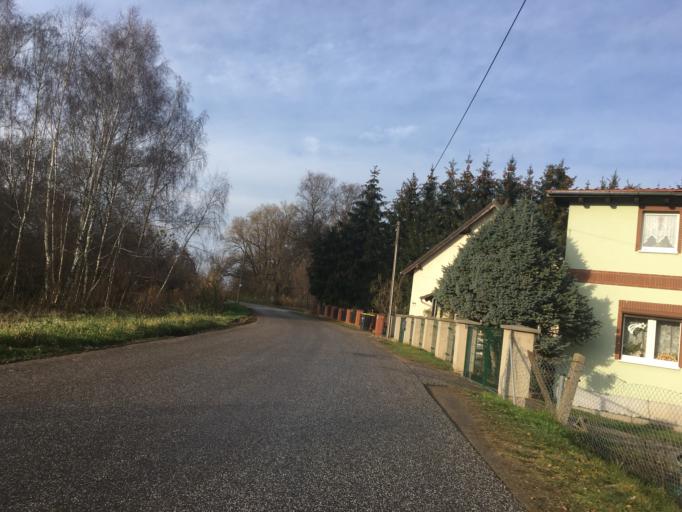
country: DE
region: Brandenburg
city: Bad Freienwalde
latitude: 52.7956
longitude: 14.0311
